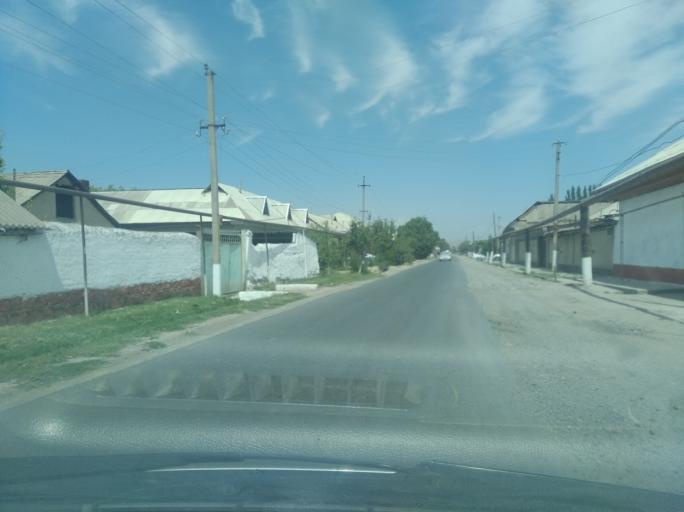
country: KG
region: Osh
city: Aravan
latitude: 40.6089
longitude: 72.4578
